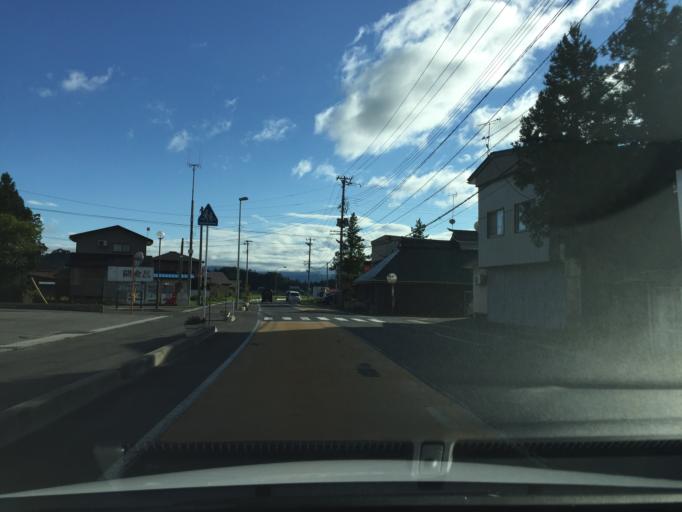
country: JP
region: Yamagata
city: Takahata
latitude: 37.9468
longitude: 140.1758
